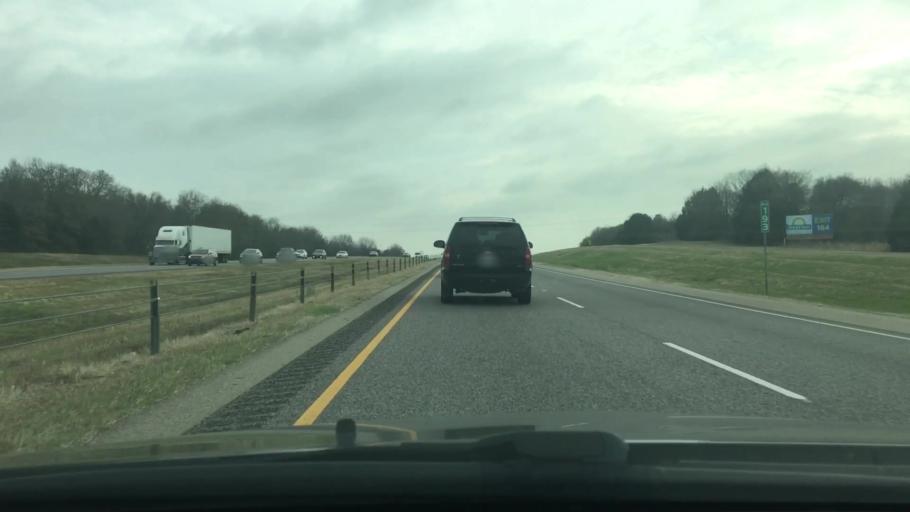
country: US
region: Texas
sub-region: Freestone County
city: Fairfield
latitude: 31.6434
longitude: -96.1590
